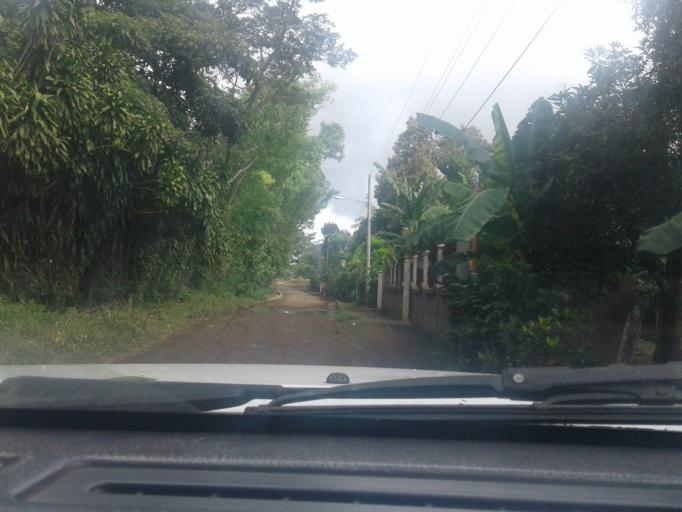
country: NI
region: Carazo
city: San Marcos
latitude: 11.8962
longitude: -86.1767
